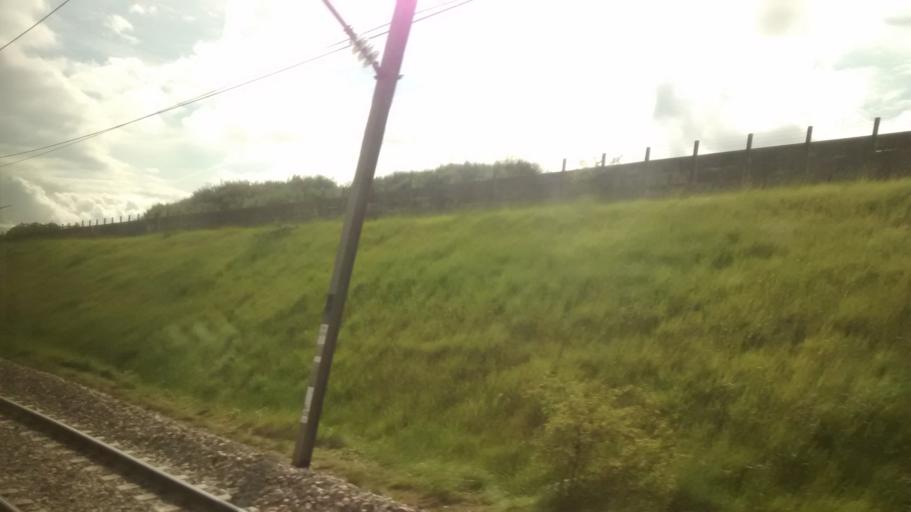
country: FR
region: Centre
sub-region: Departement d'Eure-et-Loir
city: Auneau
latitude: 48.4432
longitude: 1.7819
